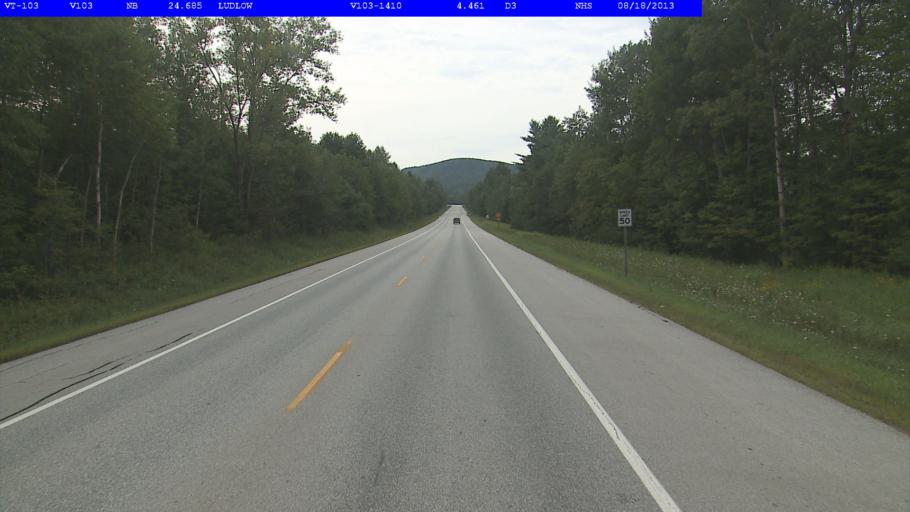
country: US
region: Vermont
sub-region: Windsor County
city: Chester
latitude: 43.4244
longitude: -72.7123
